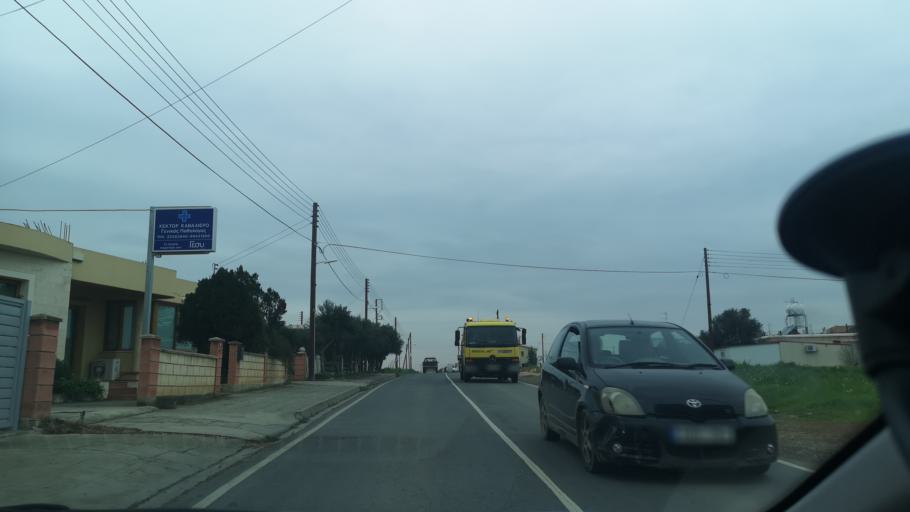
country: CY
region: Lefkosia
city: Tseri
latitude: 35.0757
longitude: 33.3170
